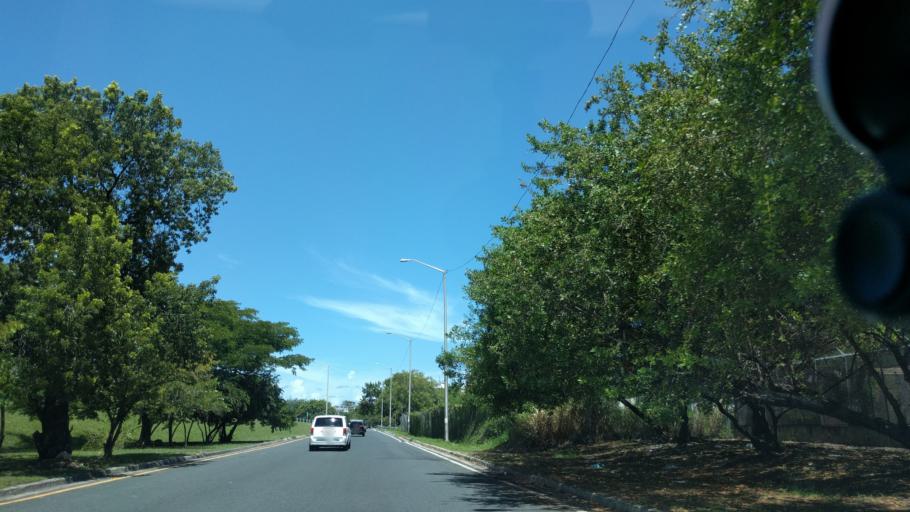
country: PR
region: San Juan
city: San Juan
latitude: 18.4374
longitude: -66.0615
